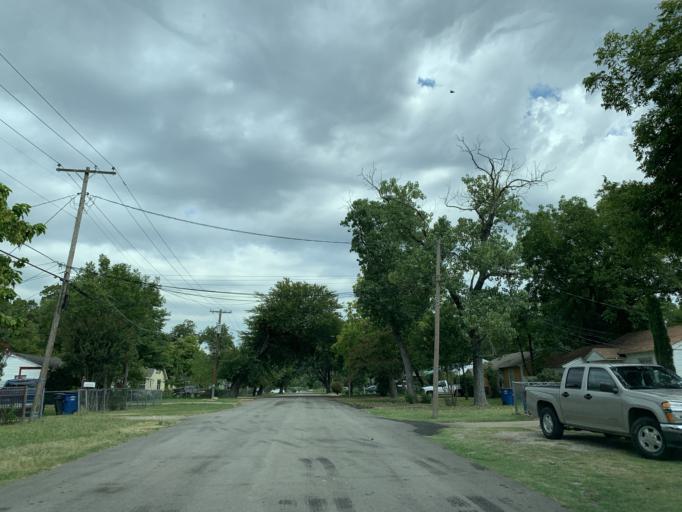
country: US
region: Texas
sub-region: Dallas County
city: DeSoto
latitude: 32.6664
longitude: -96.8267
